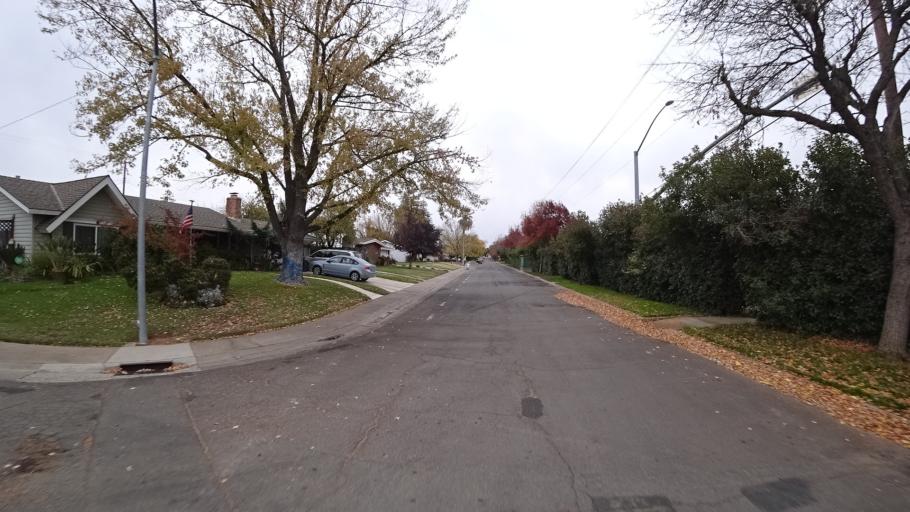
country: US
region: California
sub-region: Sacramento County
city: Citrus Heights
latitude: 38.6920
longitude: -121.2988
